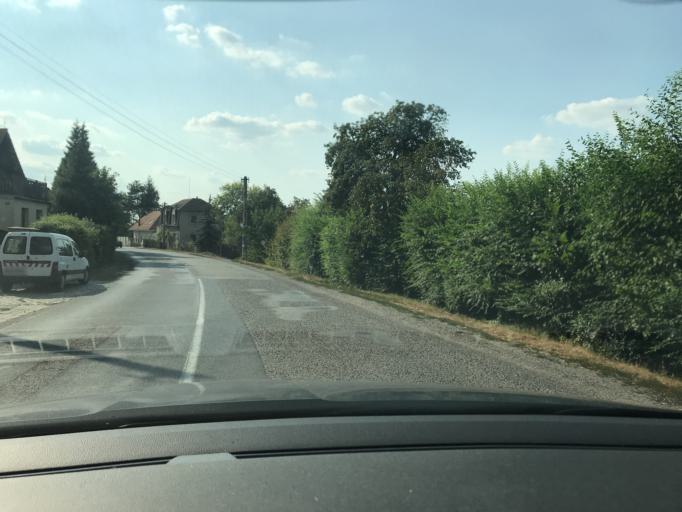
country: CZ
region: Central Bohemia
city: Kralupy nad Vltavou
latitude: 50.2314
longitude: 14.2889
